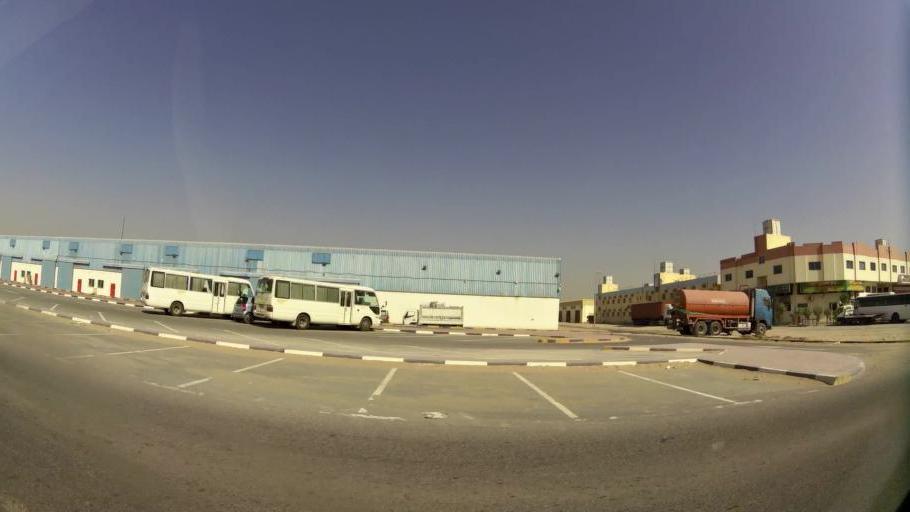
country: AE
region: Ajman
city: Ajman
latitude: 25.4252
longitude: 55.5324
